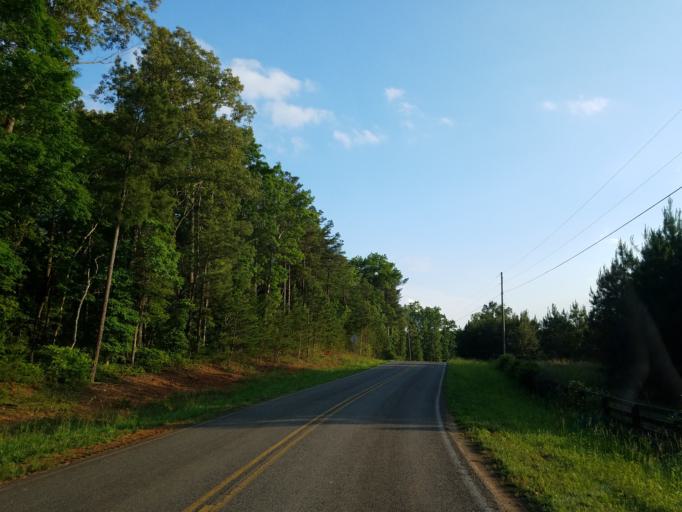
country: US
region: Georgia
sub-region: Cherokee County
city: Ball Ground
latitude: 34.3079
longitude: -84.3650
